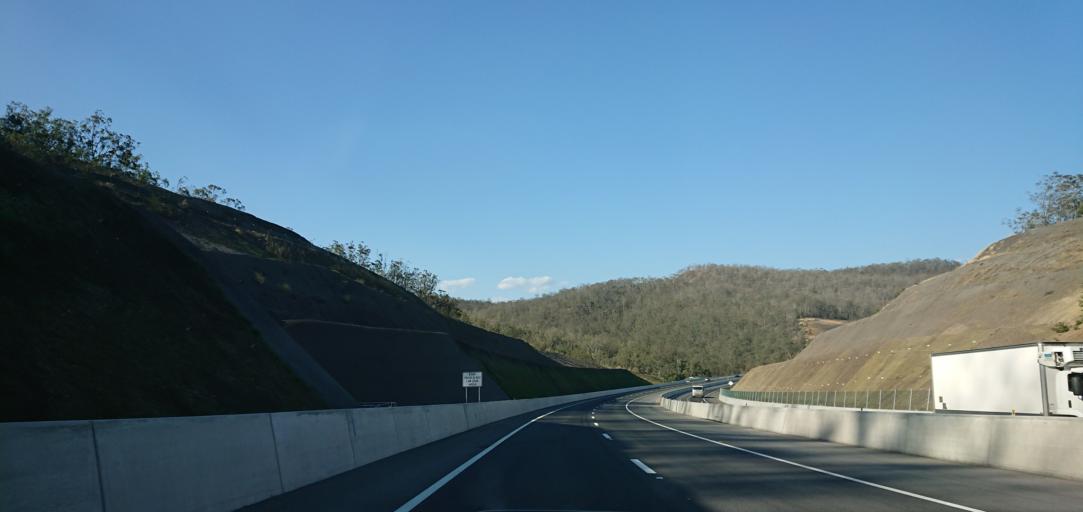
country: AU
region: Queensland
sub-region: Toowoomba
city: Wilsonton Heights
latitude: -27.5003
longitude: 151.9757
